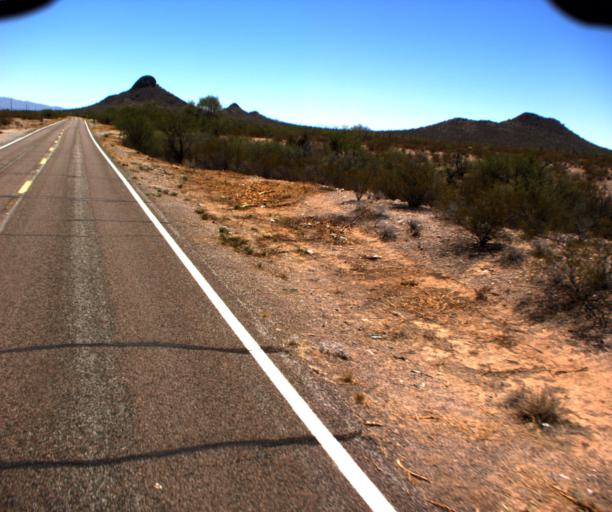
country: US
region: Arizona
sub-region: Pima County
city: Ajo
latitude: 32.2046
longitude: -112.5497
